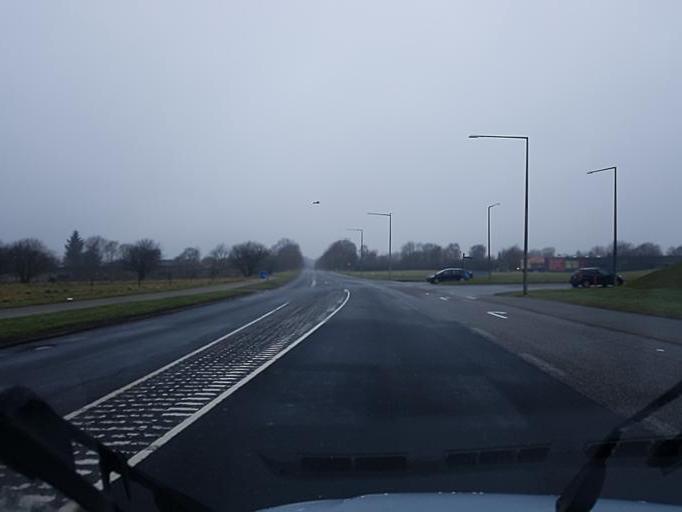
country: DK
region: South Denmark
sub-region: Esbjerg Kommune
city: Esbjerg
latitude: 55.4936
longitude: 8.4843
